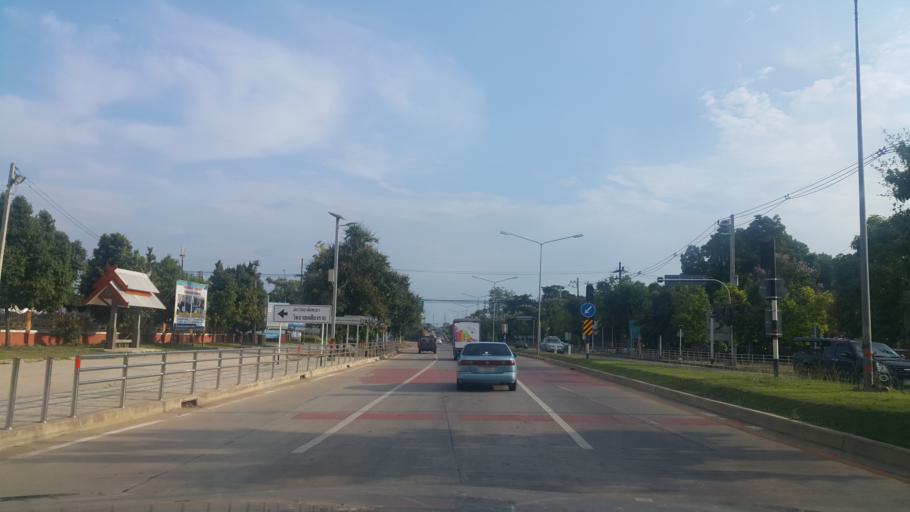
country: TH
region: Chiang Rai
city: Chiang Rai
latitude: 19.9285
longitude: 99.8635
